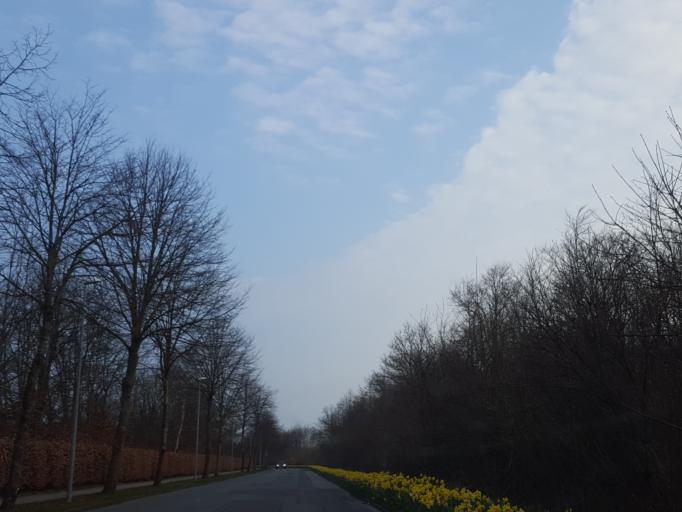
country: DK
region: South Denmark
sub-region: Esbjerg Kommune
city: Bramming
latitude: 55.4776
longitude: 8.7053
